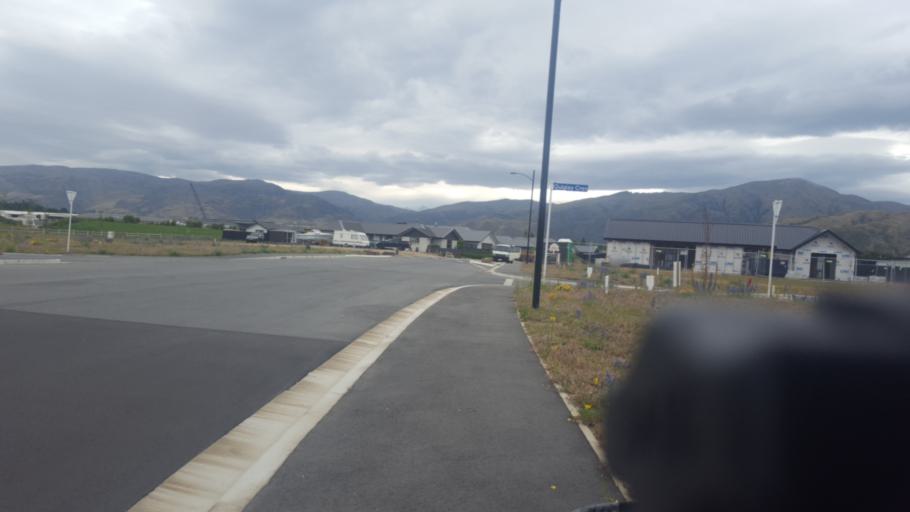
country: NZ
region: Otago
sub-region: Queenstown-Lakes District
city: Wanaka
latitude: -45.0478
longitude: 169.1907
